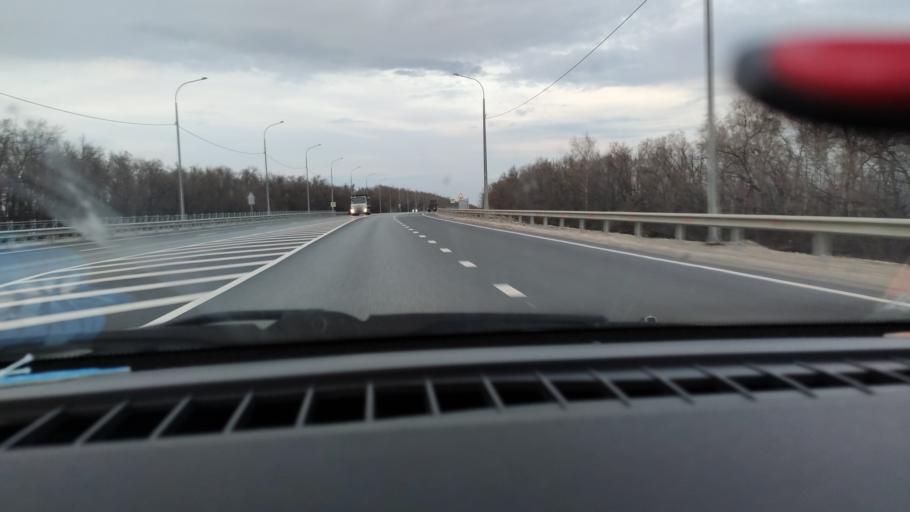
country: RU
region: Saratov
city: Yelshanka
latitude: 51.8985
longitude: 46.5365
